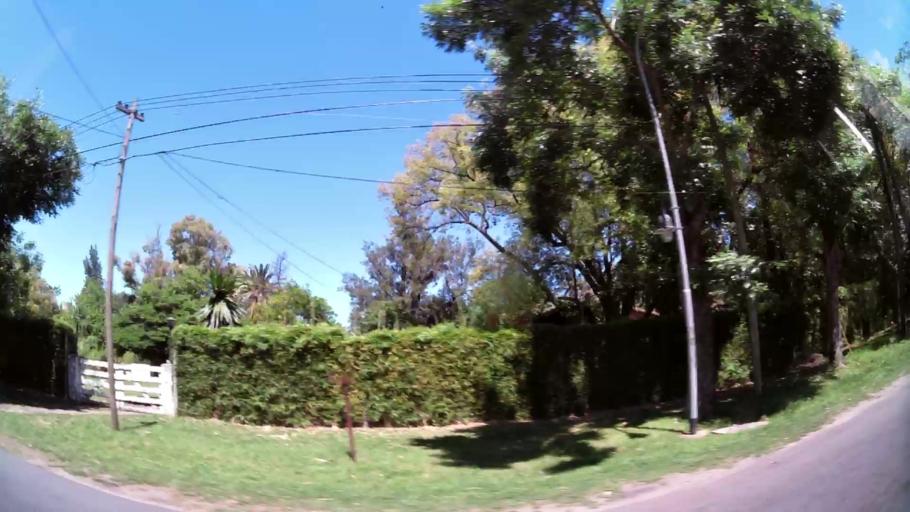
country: AR
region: Buenos Aires
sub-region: Partido de Tigre
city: Tigre
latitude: -34.4935
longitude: -58.6428
